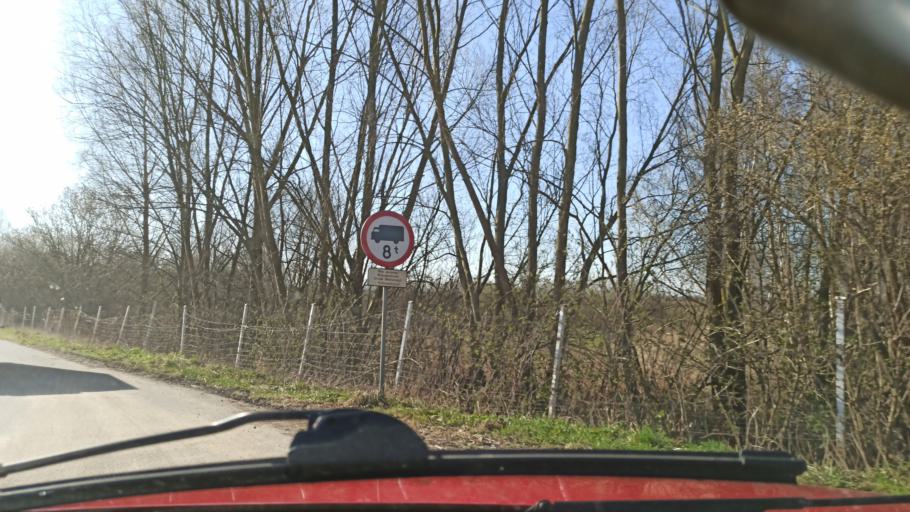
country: PL
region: Warmian-Masurian Voivodeship
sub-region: Powiat elblaski
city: Elblag
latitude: 54.1386
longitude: 19.4055
